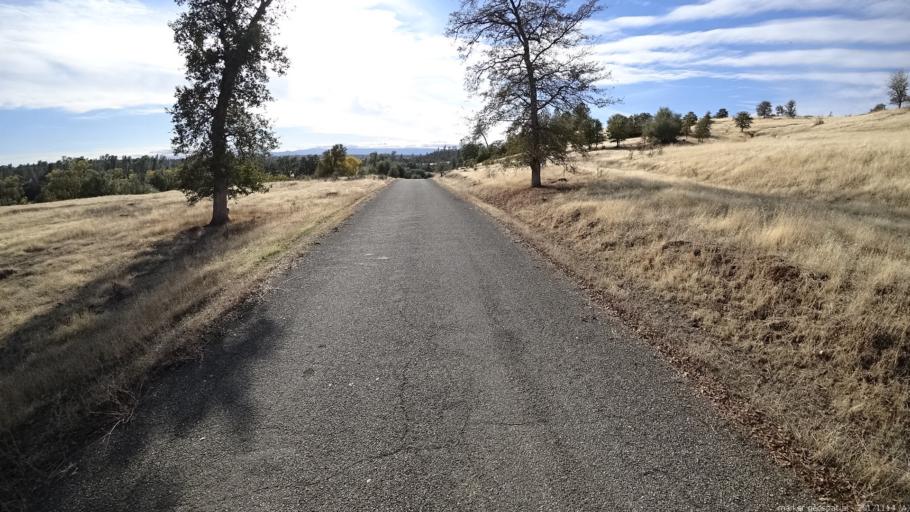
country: US
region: California
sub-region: Shasta County
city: Shasta
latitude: 40.3815
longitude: -122.5500
